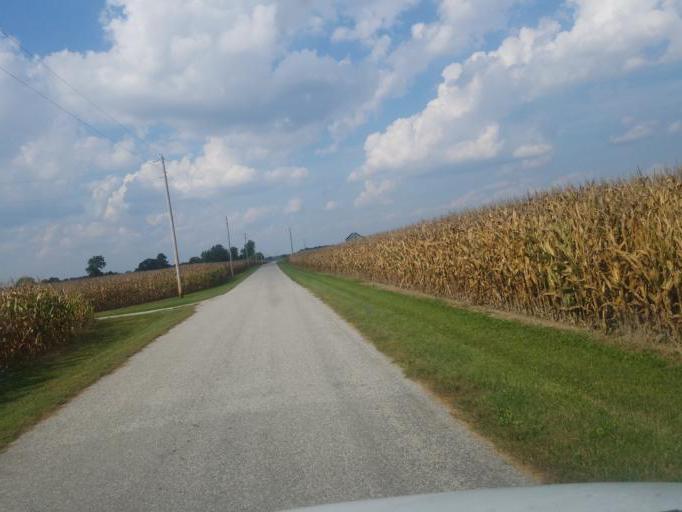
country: US
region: Ohio
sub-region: Hardin County
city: Kenton
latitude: 40.7204
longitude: -83.6144
